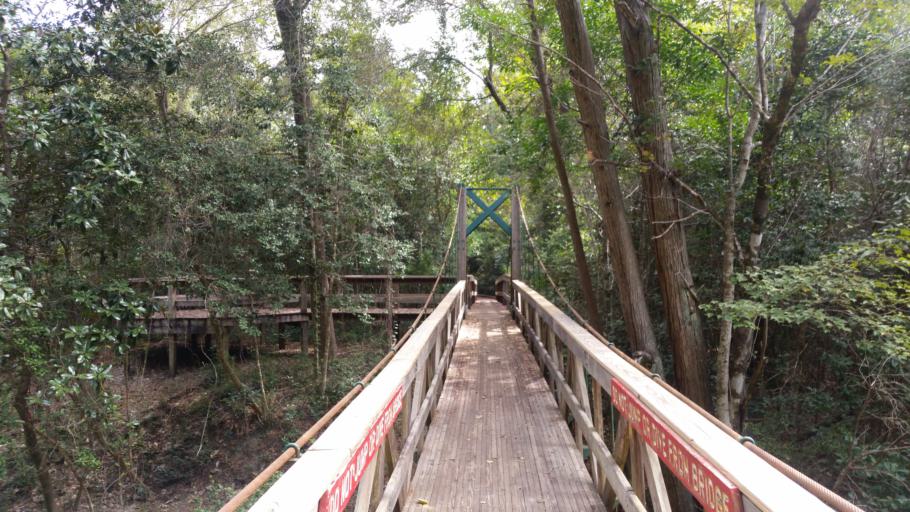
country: US
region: Florida
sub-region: Santa Rosa County
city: Point Baker
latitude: 30.8599
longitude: -86.8509
